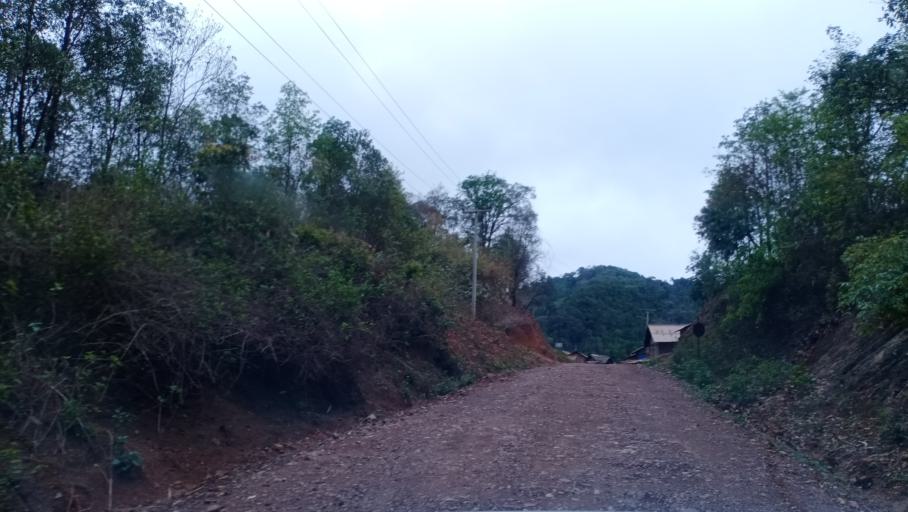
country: LA
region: Phongsali
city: Phongsali
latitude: 21.3452
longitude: 102.0905
